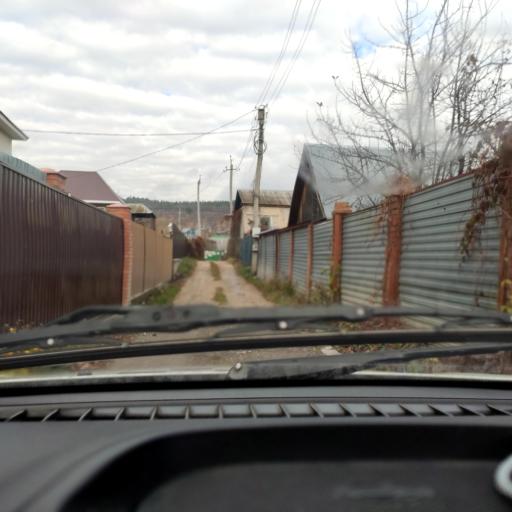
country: RU
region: Samara
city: Zhigulevsk
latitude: 53.4654
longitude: 49.6429
